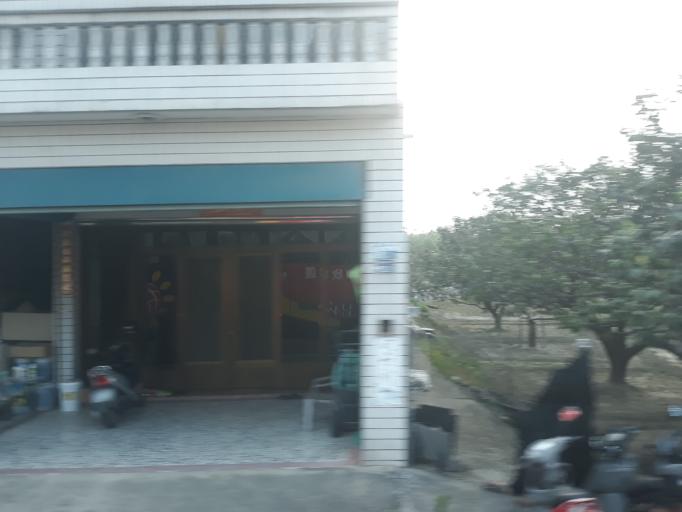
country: TW
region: Taiwan
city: Xinying
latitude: 23.1848
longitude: 120.2395
